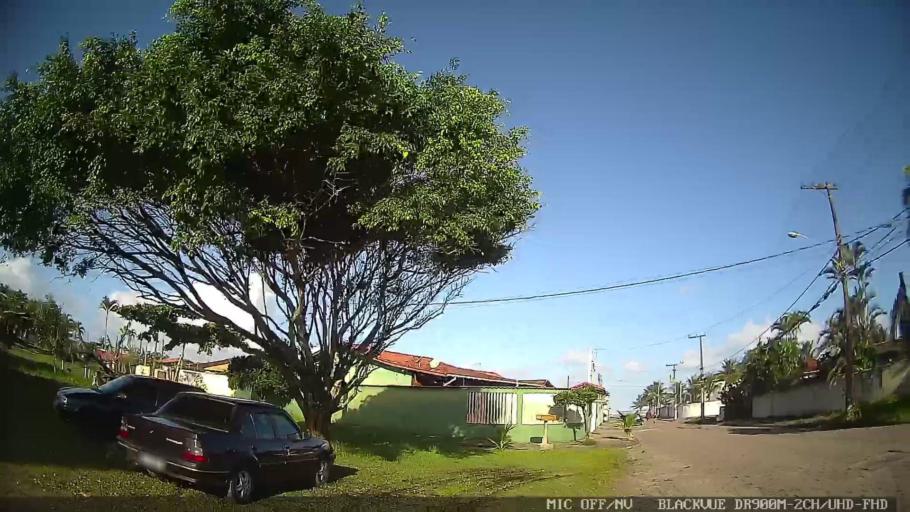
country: BR
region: Sao Paulo
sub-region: Itanhaem
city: Itanhaem
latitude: -24.1532
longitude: -46.7306
